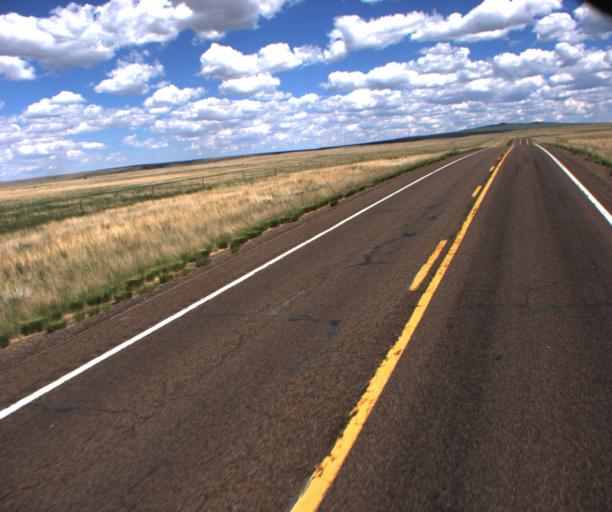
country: US
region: Arizona
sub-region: Apache County
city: Springerville
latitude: 34.1900
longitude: -109.3486
